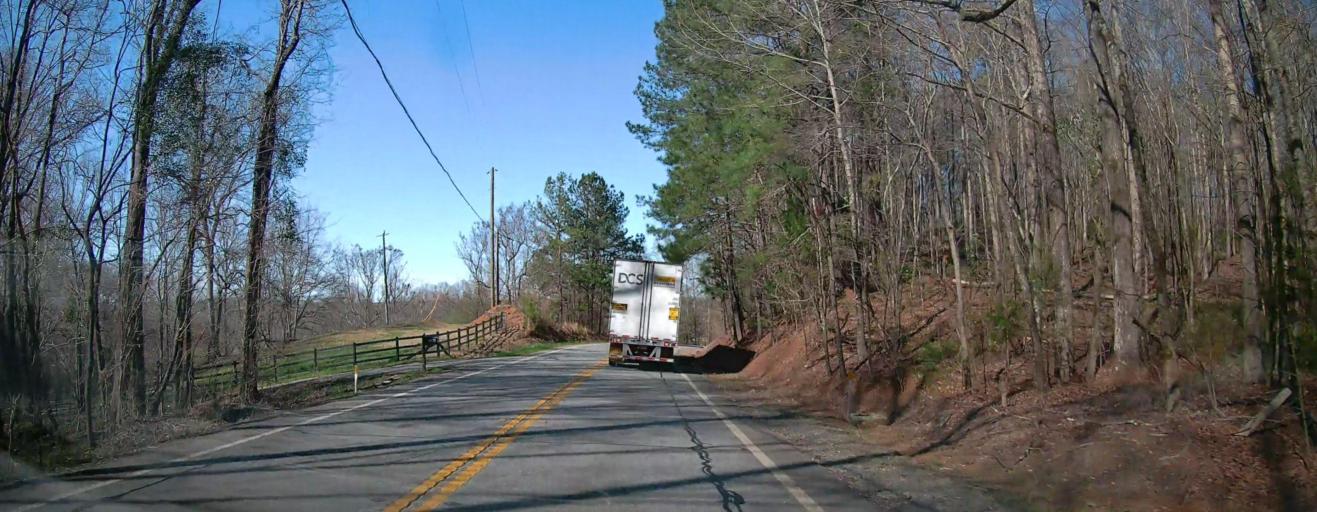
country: US
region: Georgia
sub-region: Butts County
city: Indian Springs
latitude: 33.2086
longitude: -83.9347
